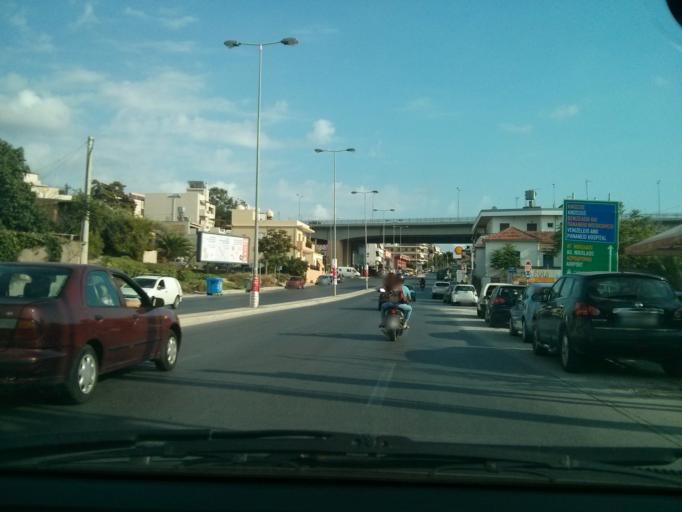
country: GR
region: Crete
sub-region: Nomos Irakleiou
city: Irakleion
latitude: 35.3219
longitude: 25.1426
